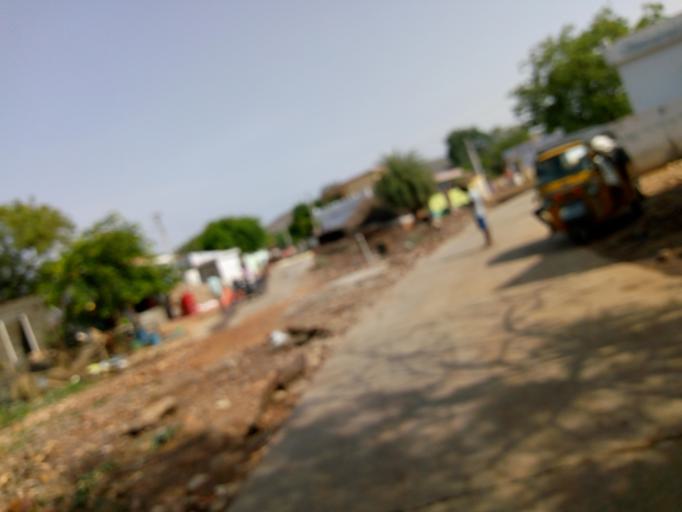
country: IN
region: Andhra Pradesh
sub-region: Prakasam
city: Cumbum
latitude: 15.7163
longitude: 79.0775
